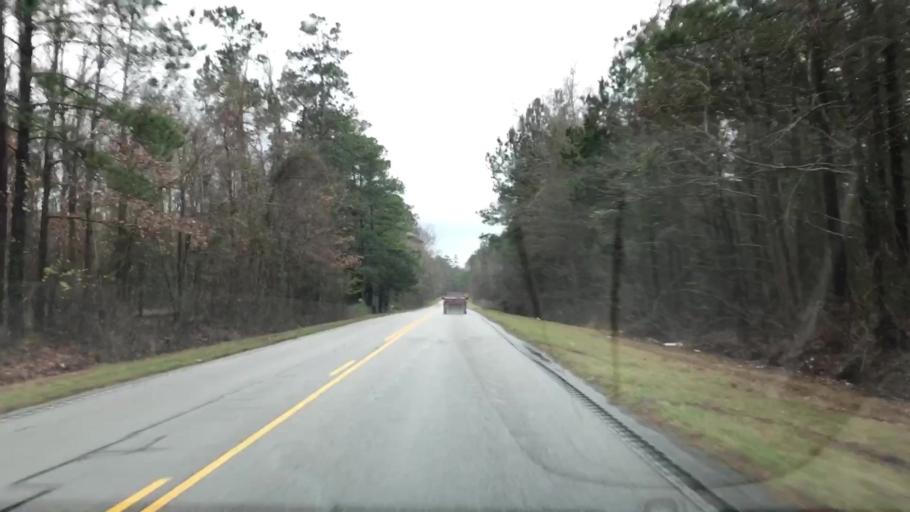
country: US
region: South Carolina
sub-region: Williamsburg County
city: Andrews
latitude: 33.5248
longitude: -79.4906
